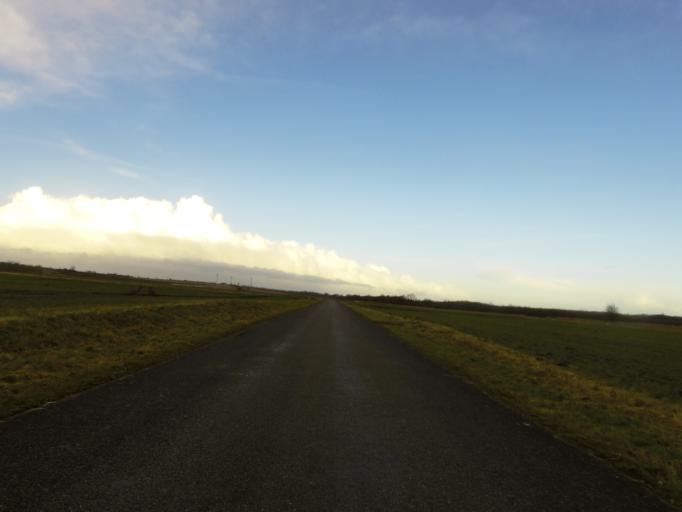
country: DK
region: South Denmark
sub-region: Haderslev Kommune
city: Gram
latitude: 55.2444
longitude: 9.0754
